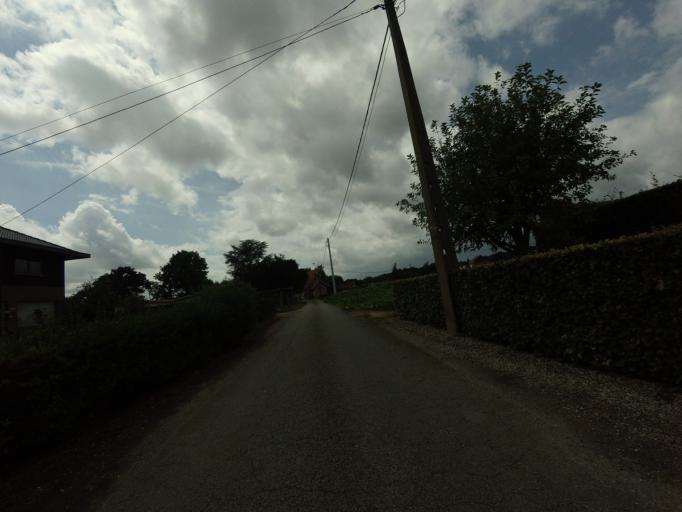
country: BE
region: Flanders
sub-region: Provincie Antwerpen
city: Sint-Katelijne-Waver
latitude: 51.0490
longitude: 4.5076
